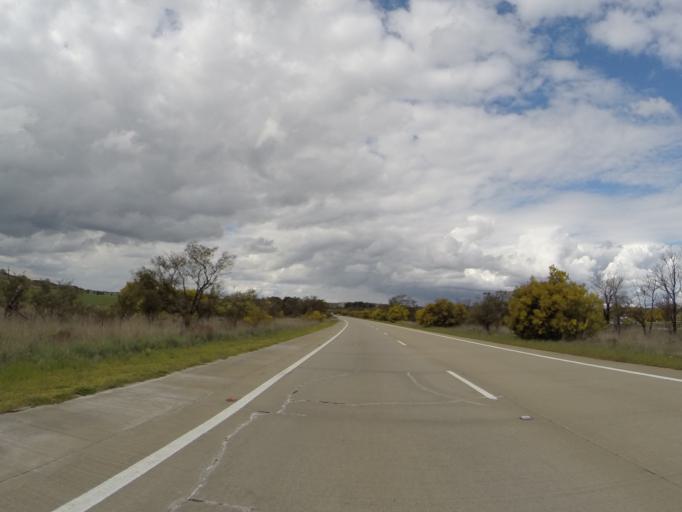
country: AU
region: New South Wales
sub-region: Goulburn Mulwaree
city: Goulburn
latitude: -34.8161
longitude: 149.4599
